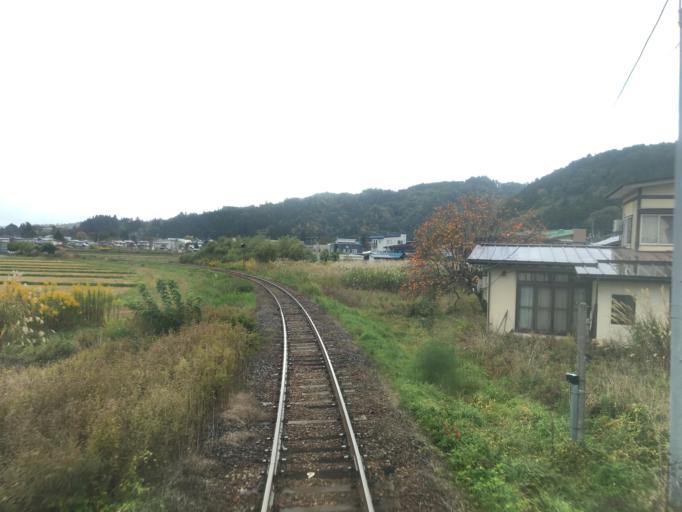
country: JP
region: Yamagata
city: Takahata
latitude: 38.0720
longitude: 140.1317
